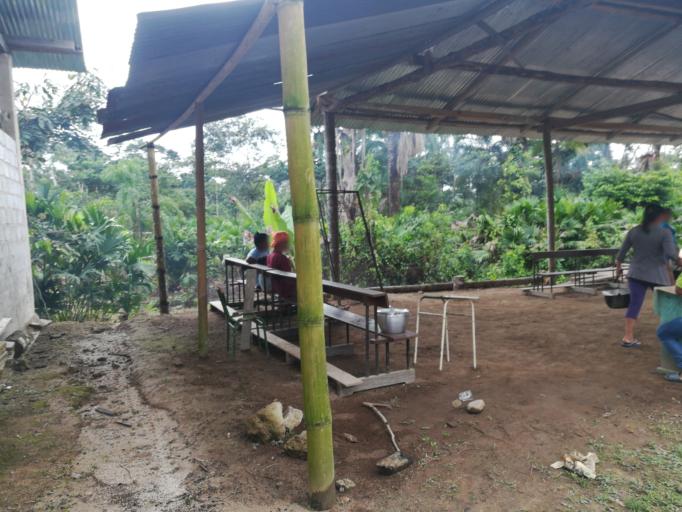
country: EC
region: Napo
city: Archidona
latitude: -0.9105
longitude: -77.8254
